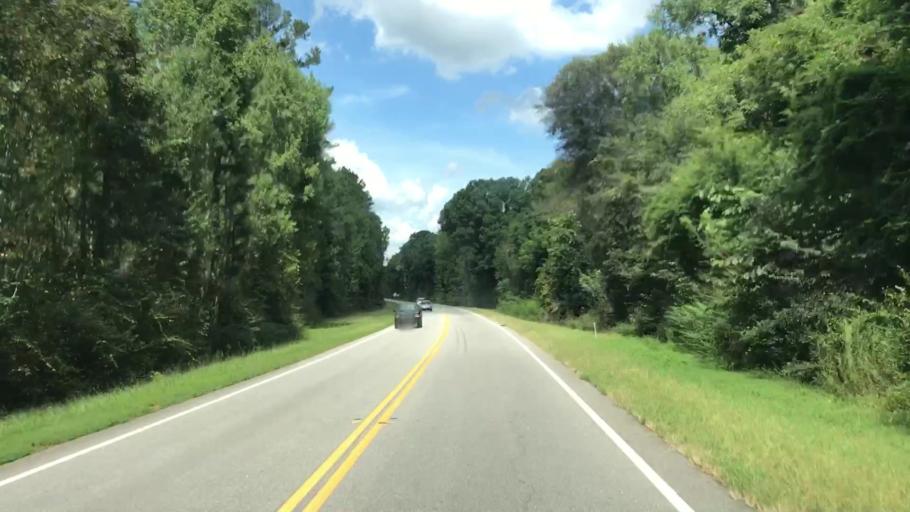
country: US
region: Georgia
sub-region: Greene County
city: Greensboro
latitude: 33.6954
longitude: -83.2777
